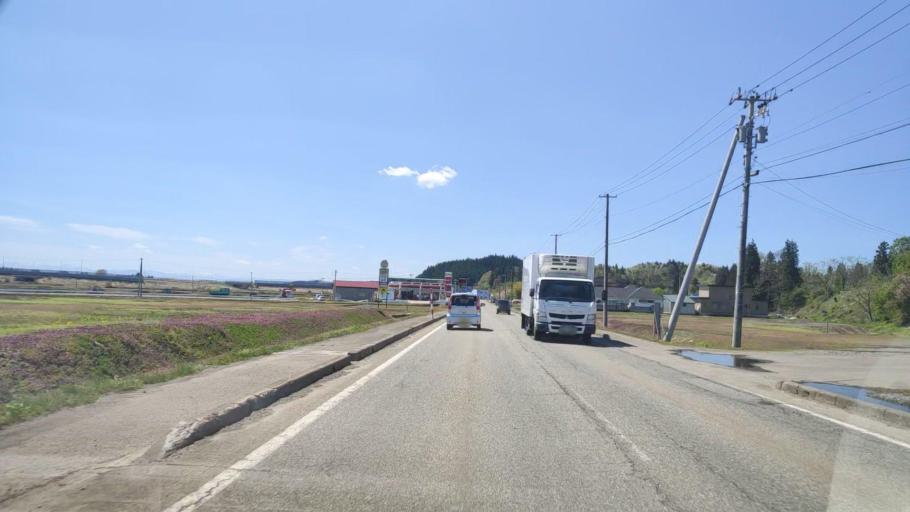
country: JP
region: Akita
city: Omagari
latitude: 39.4367
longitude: 140.4471
